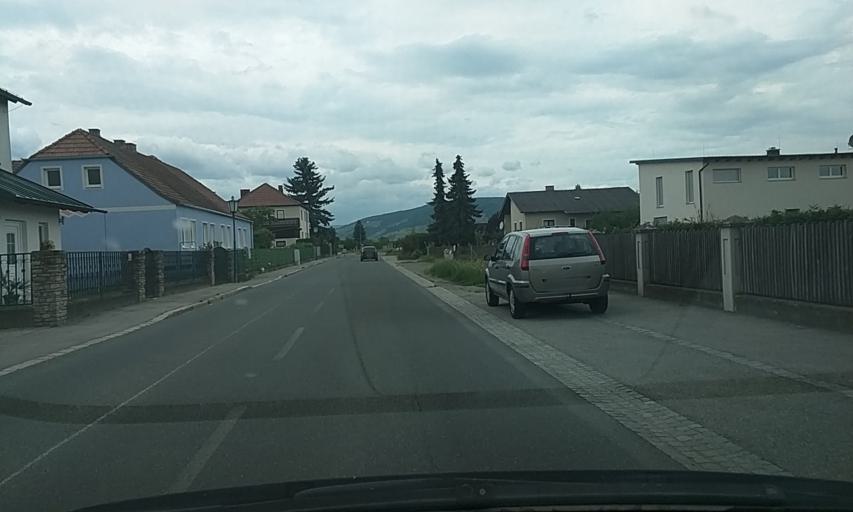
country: AT
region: Lower Austria
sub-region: Politischer Bezirk Krems
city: Weinzierl bei Krems
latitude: 48.3858
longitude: 15.6048
